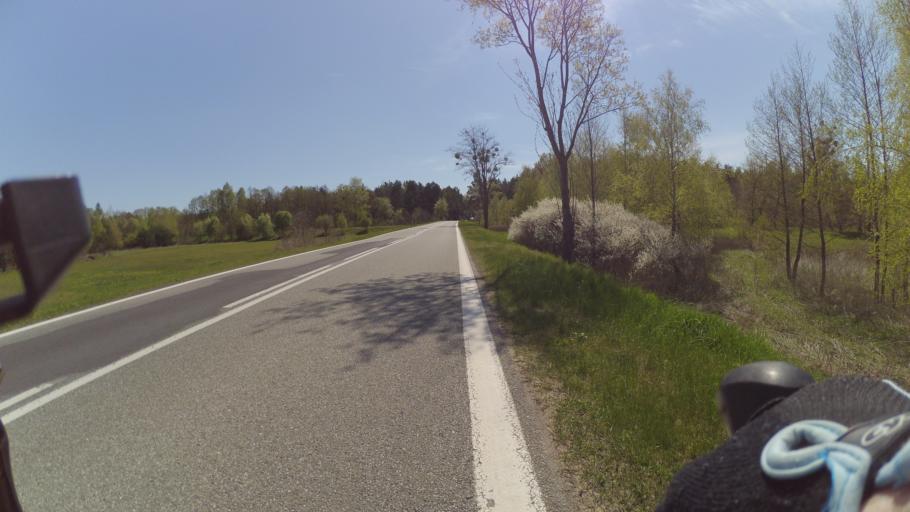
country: PL
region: Masovian Voivodeship
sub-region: Powiat plonski
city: Czerwinsk Nad Wisla
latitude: 52.3702
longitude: 20.3085
